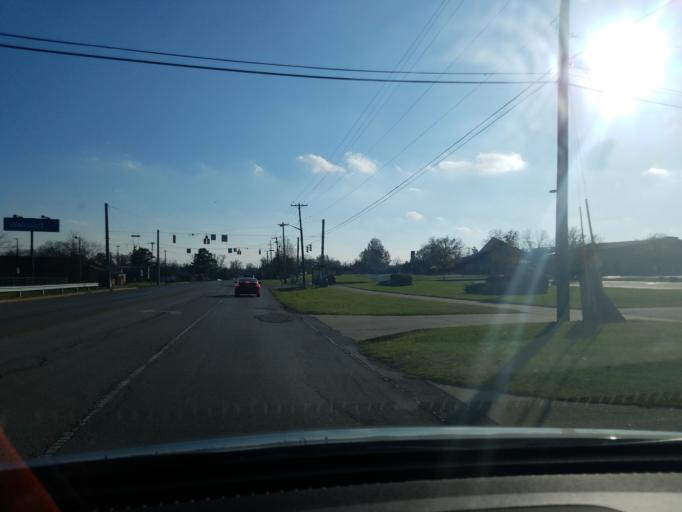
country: US
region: Indiana
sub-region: Floyd County
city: New Albany
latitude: 38.3189
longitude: -85.8204
